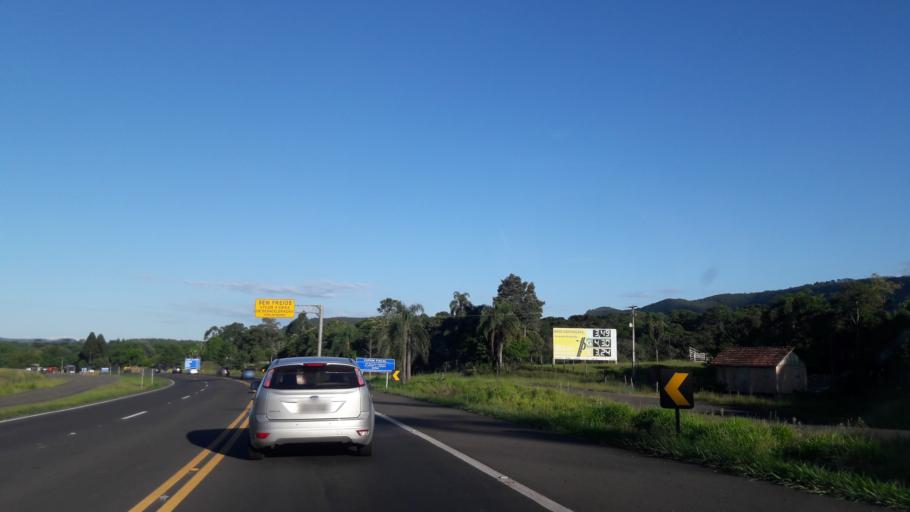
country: BR
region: Parana
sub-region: Prudentopolis
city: Prudentopolis
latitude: -25.3132
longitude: -51.1757
